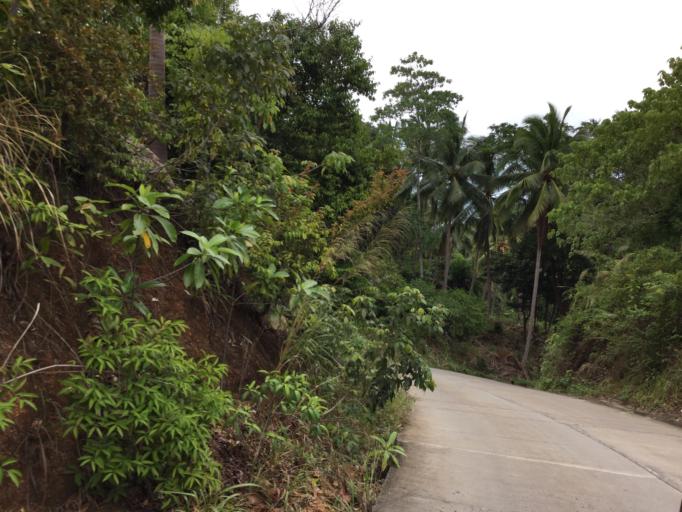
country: TH
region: Nakhon Si Thammarat
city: Ko Pha Ngan
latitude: 9.7378
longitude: 100.0674
